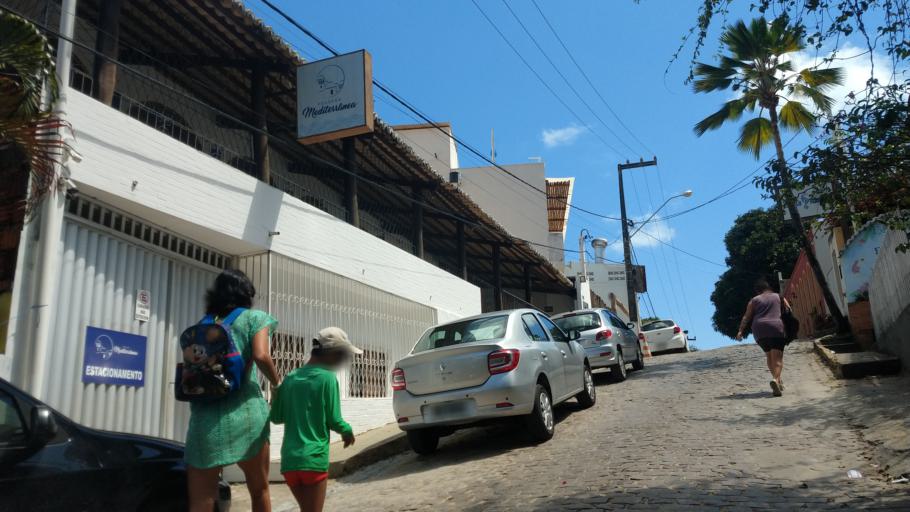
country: BR
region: Rio Grande do Norte
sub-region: Ares
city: Ares
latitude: -6.2299
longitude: -35.0498
